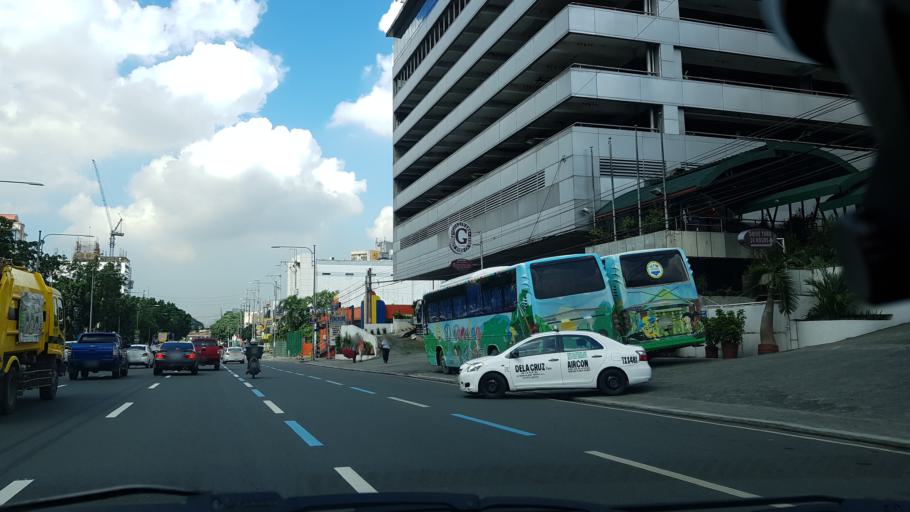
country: PH
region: Calabarzon
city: Del Monte
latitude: 14.6394
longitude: 121.0296
